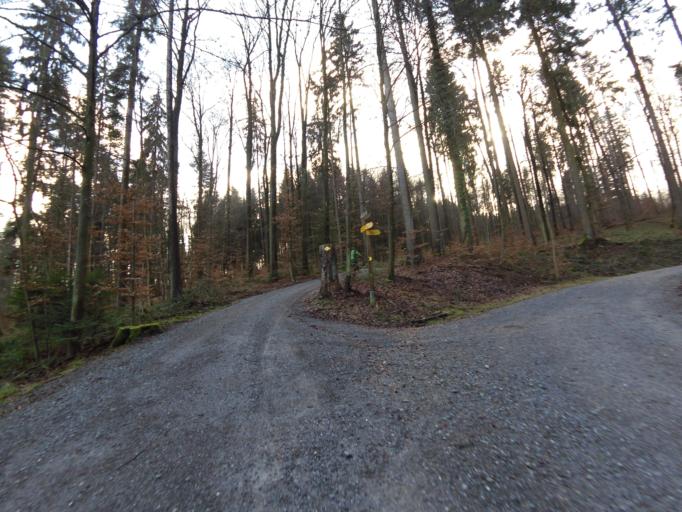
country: CH
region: Zurich
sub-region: Bezirk Zuerich
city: Zuerich (Kreis 9)
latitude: 47.3748
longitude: 8.4702
